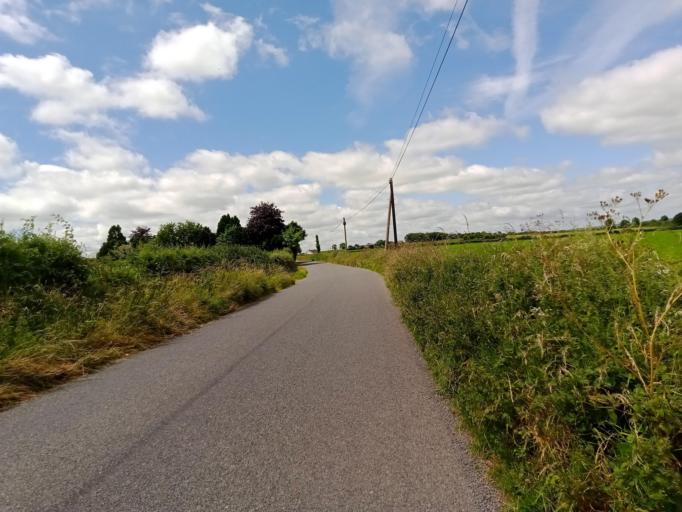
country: IE
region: Leinster
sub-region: Kilkenny
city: Callan
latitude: 52.5457
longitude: -7.4039
